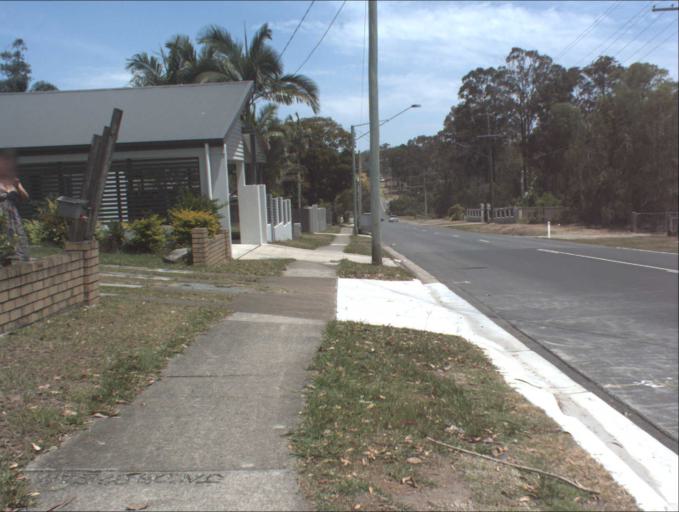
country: AU
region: Queensland
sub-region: Logan
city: Rochedale South
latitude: -27.5893
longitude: 153.1369
